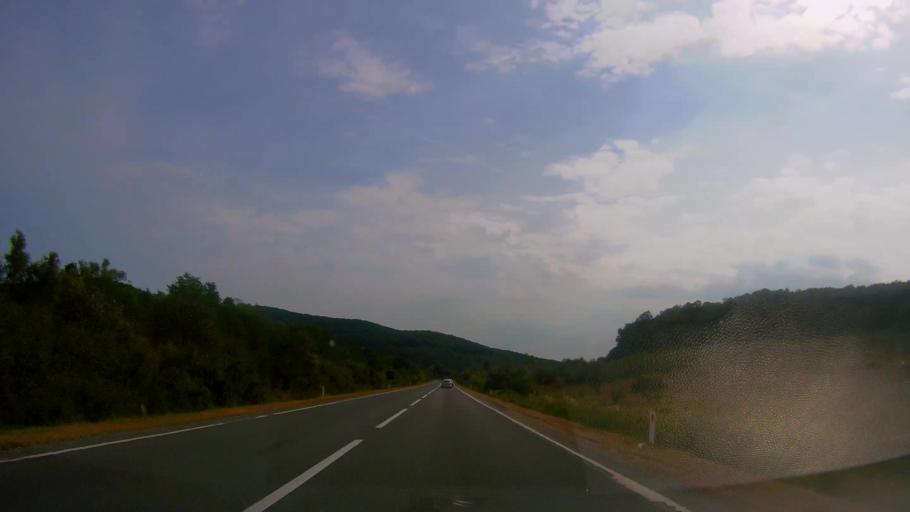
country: RO
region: Salaj
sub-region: Comuna Zimbor
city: Zimbor
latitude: 46.9679
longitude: 23.2845
